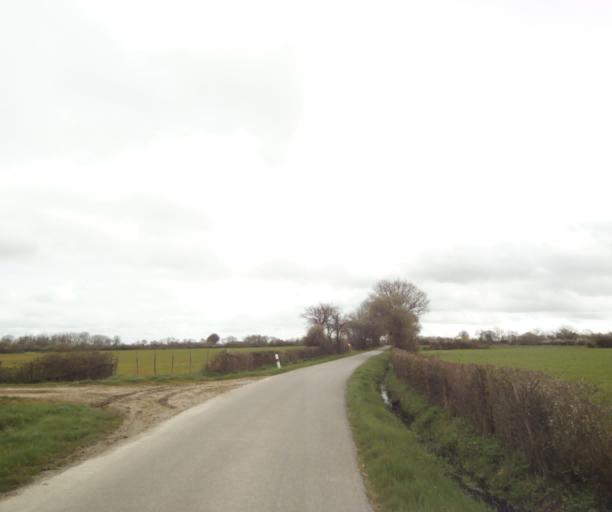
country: FR
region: Pays de la Loire
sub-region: Departement de la Loire-Atlantique
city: Bouvron
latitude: 47.4429
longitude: -1.8723
